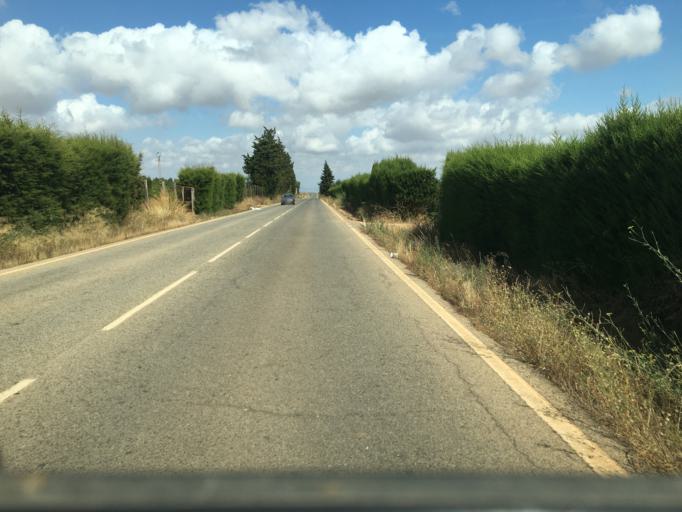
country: ES
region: Murcia
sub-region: Murcia
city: La Union
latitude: 37.6456
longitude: -0.8734
